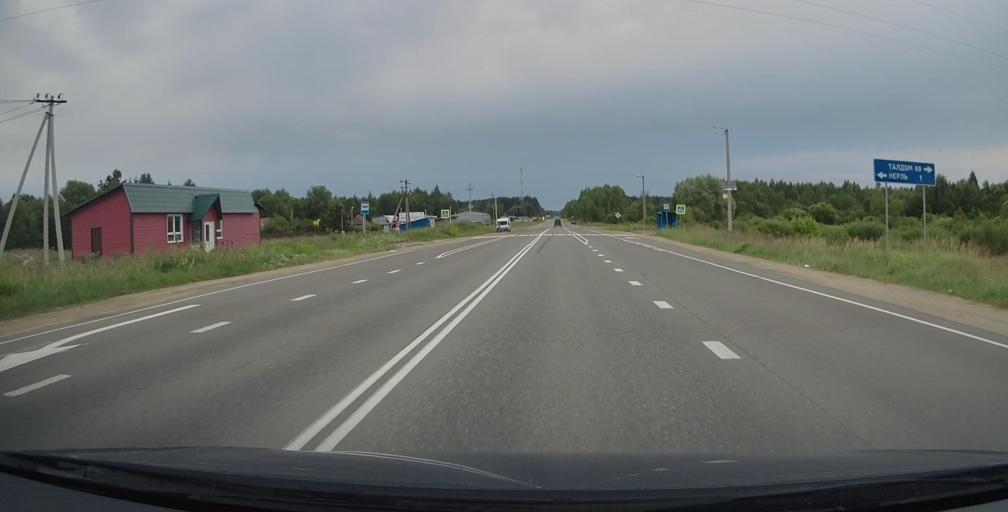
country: RU
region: Tverskaya
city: Kalyazin
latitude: 57.0282
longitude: 37.9840
